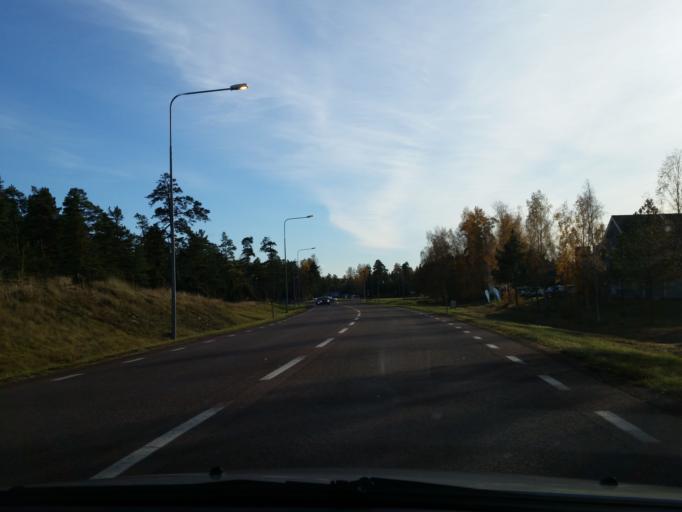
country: AX
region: Mariehamns stad
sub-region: Mariehamn
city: Mariehamn
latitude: 60.1245
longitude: 19.9337
